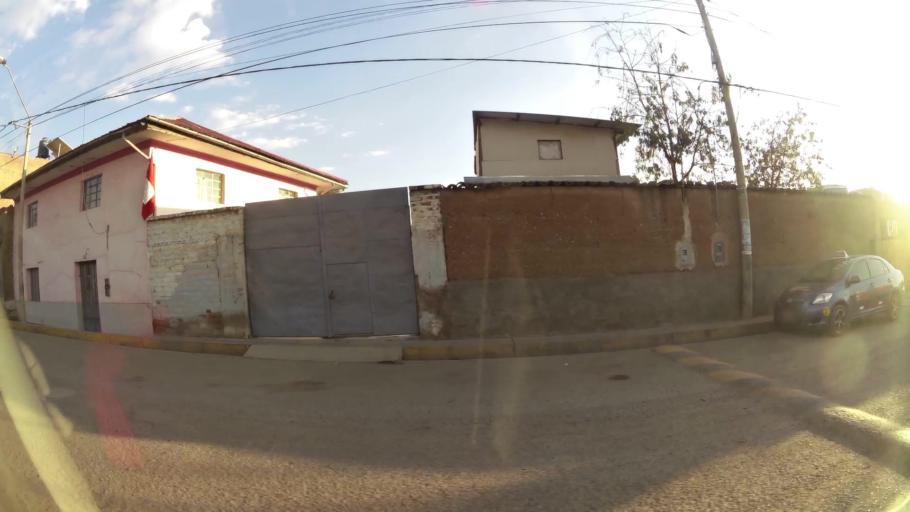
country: PE
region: Junin
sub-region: Provincia de Huancayo
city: El Tambo
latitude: -12.0427
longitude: -75.2209
